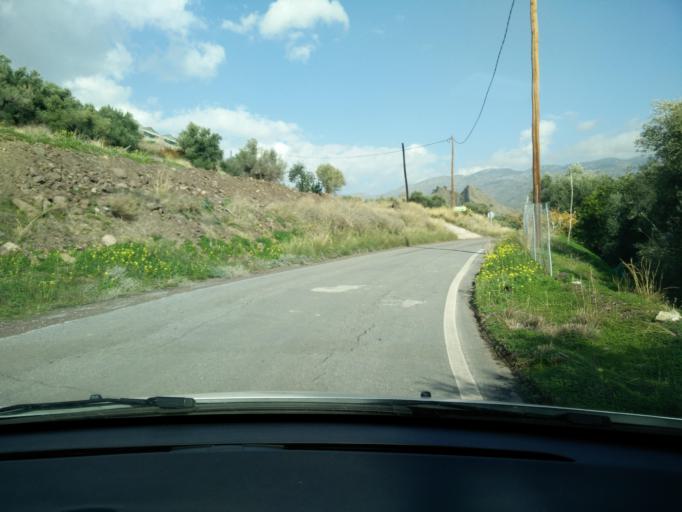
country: GR
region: Crete
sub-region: Nomos Lasithiou
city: Gra Liyia
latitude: 35.0283
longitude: 25.5794
